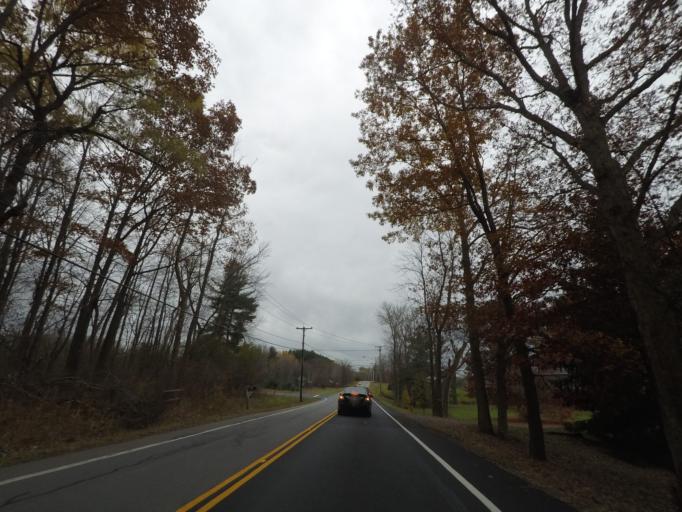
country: US
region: New York
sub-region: Schenectady County
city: Niskayuna
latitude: 42.8328
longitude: -73.8231
